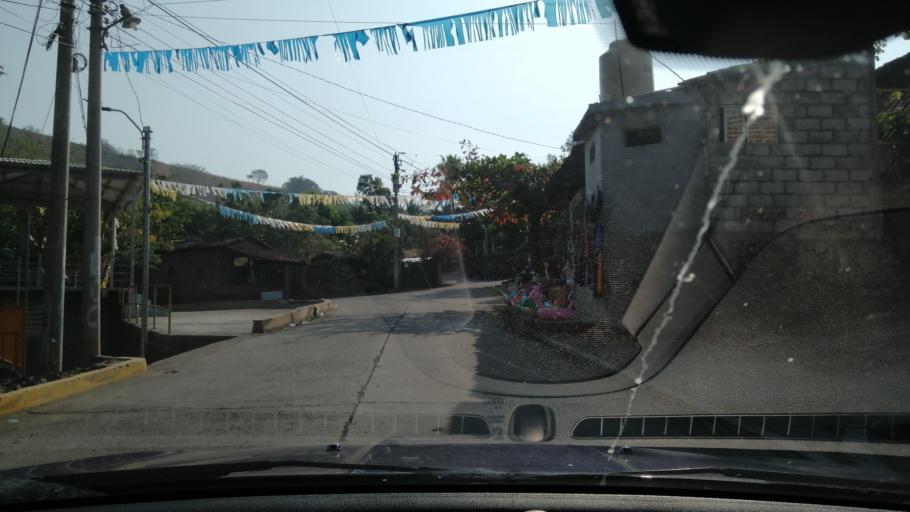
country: SV
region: Santa Ana
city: Texistepeque
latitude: 14.2215
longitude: -89.4553
